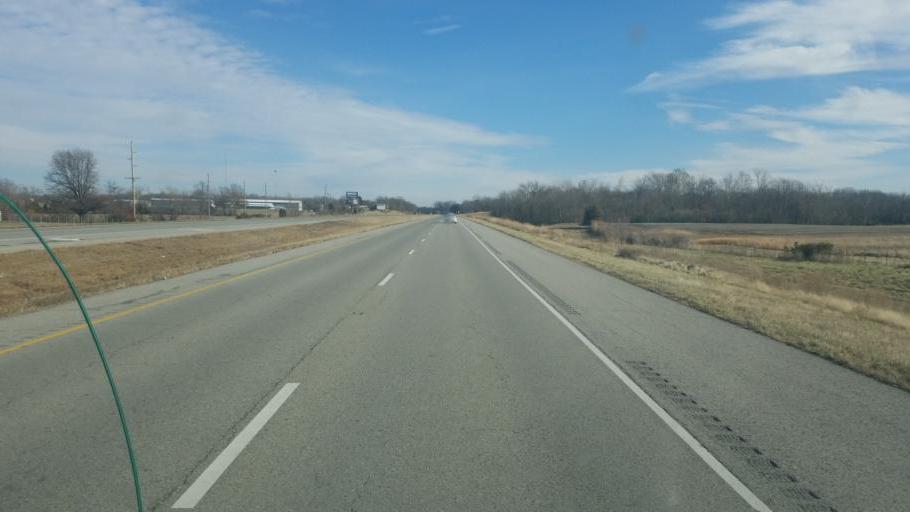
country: US
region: Illinois
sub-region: Williamson County
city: Marion
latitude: 37.7295
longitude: -88.8364
